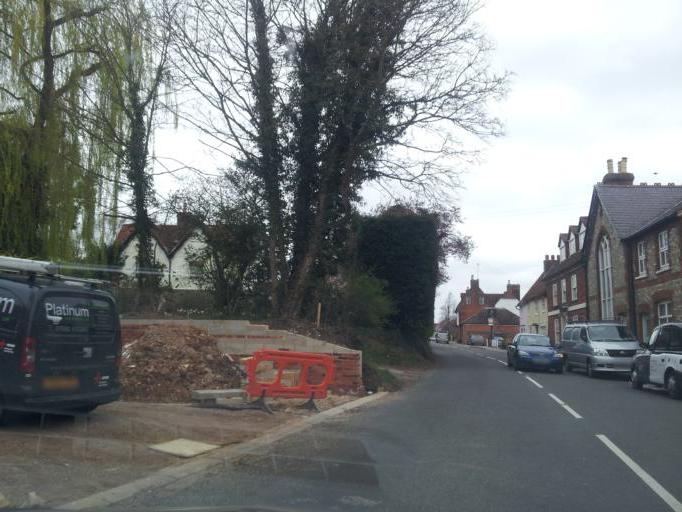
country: GB
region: England
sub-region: Hertfordshire
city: Buntingford
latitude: 51.9078
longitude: 0.0241
